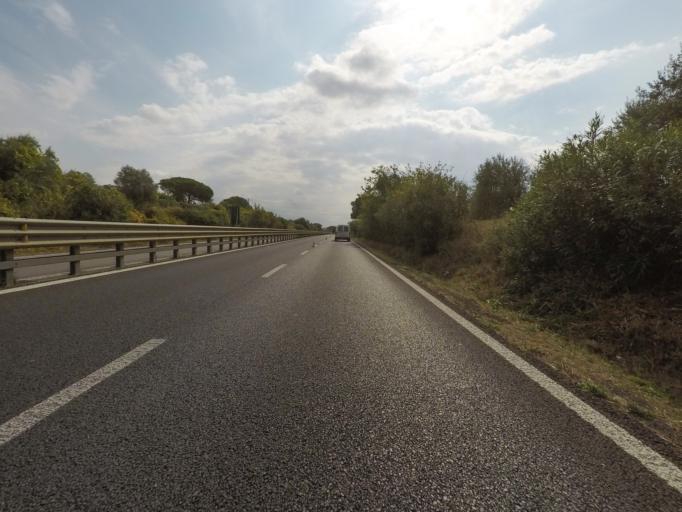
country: IT
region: Tuscany
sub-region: Provincia di Grosseto
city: Grosseto
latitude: 42.7251
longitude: 11.1372
